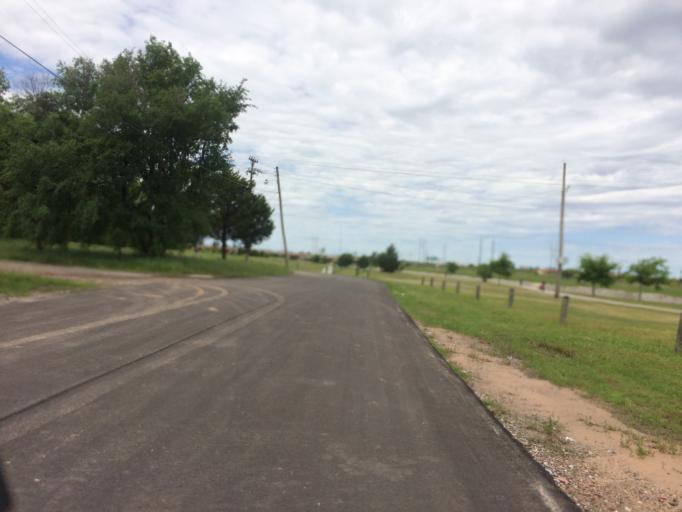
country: US
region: Oklahoma
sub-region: Oklahoma County
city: Oklahoma City
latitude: 35.4562
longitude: -97.5672
